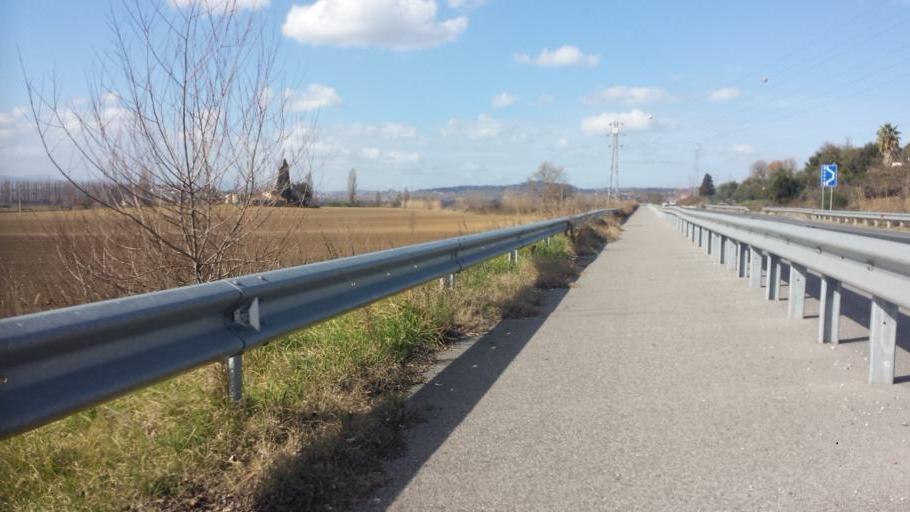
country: IT
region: Umbria
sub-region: Provincia di Terni
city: Terni
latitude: 42.5735
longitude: 12.5996
